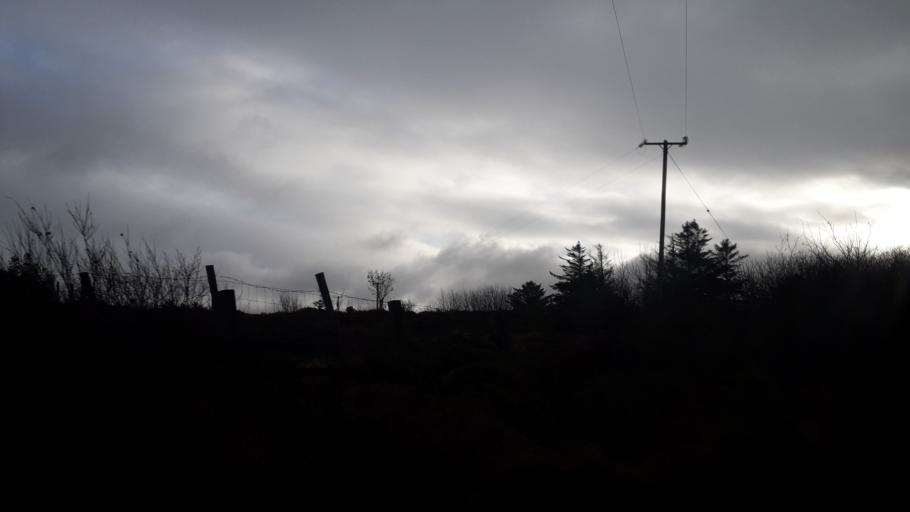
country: IE
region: Ulster
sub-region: County Donegal
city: Buncrana
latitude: 55.1738
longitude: -7.5807
